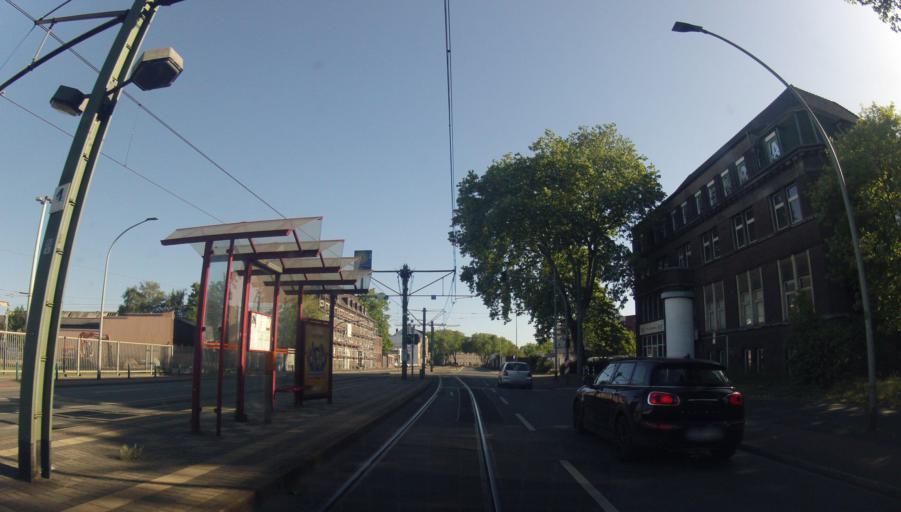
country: DE
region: North Rhine-Westphalia
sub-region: Regierungsbezirk Dusseldorf
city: Hochfeld
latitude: 51.4096
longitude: 6.7682
